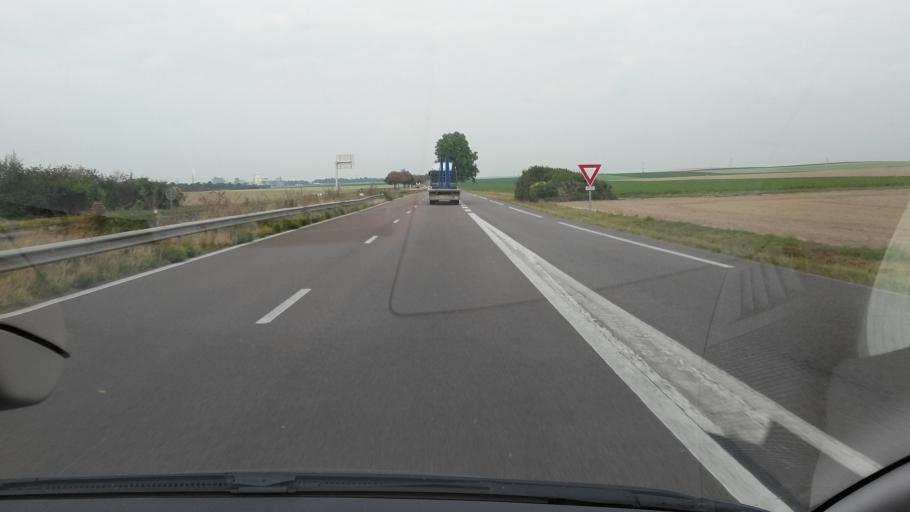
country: FR
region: Champagne-Ardenne
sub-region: Departement de la Marne
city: Witry-les-Reims
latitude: 49.3161
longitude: 4.1524
